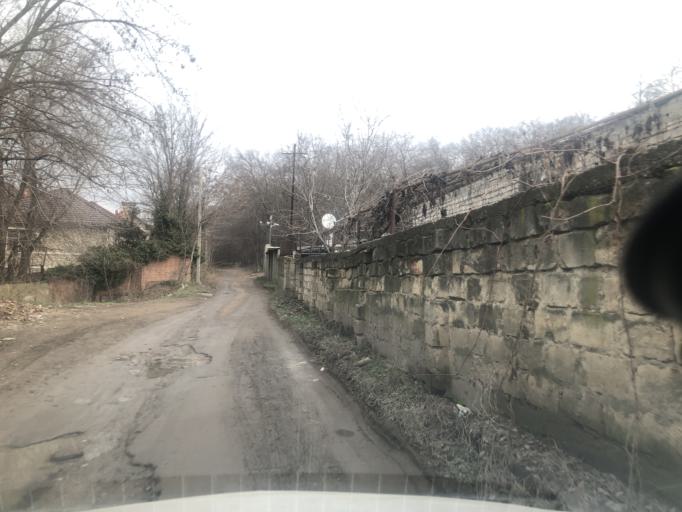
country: MD
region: Chisinau
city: Chisinau
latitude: 47.0311
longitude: 28.8692
